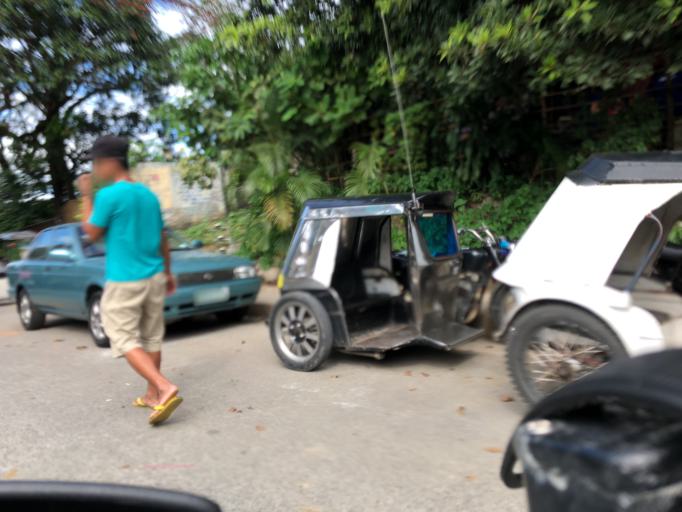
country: PH
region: Central Luzon
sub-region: Province of Bulacan
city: San Jose del Monte
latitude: 14.7629
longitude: 121.0499
